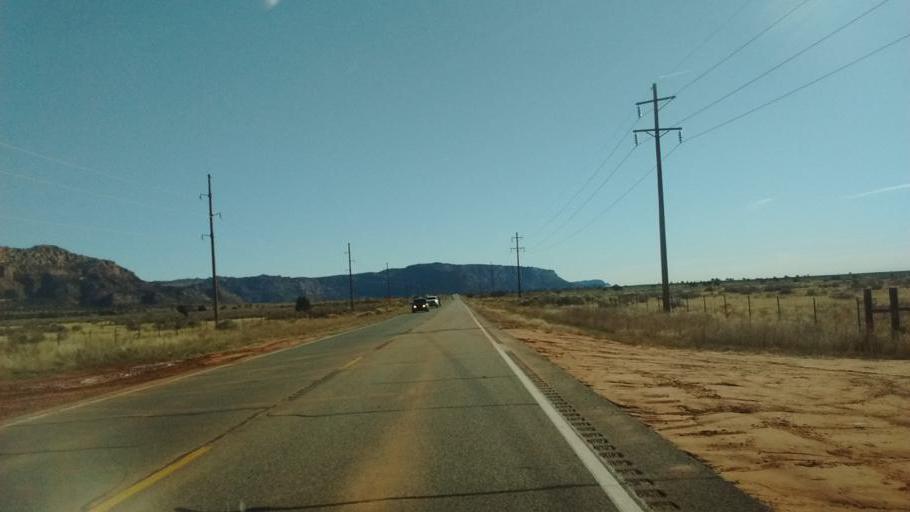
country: US
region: Arizona
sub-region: Mohave County
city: Colorado City
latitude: 37.0172
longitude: -113.0293
